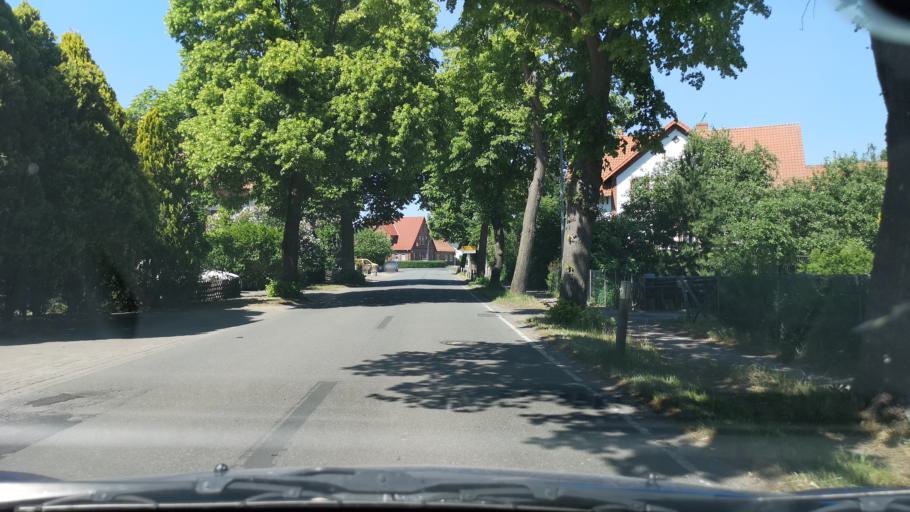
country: DE
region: Lower Saxony
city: Garbsen-Mitte
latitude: 52.4669
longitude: 9.6184
